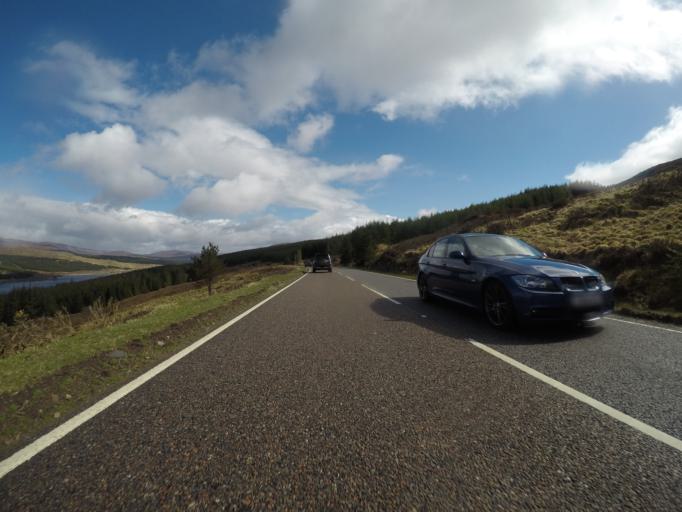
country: GB
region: Scotland
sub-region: Highland
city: Spean Bridge
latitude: 57.1022
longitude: -4.9901
